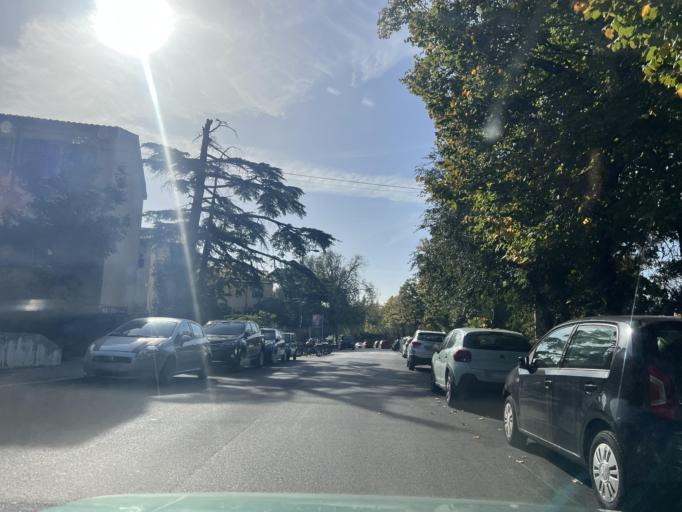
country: IT
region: Friuli Venezia Giulia
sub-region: Provincia di Trieste
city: Domio
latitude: 45.6174
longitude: 13.8255
